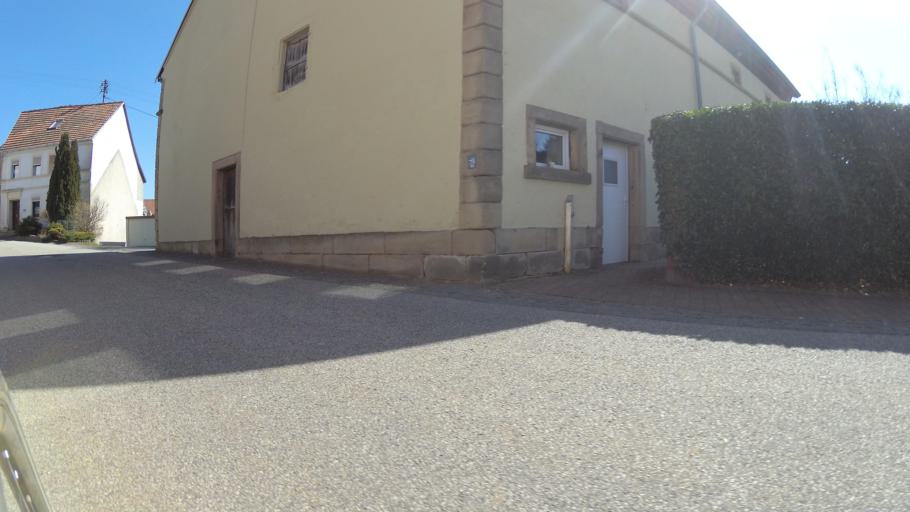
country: DE
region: Rheinland-Pfalz
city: Korborn
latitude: 49.5632
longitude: 7.3702
